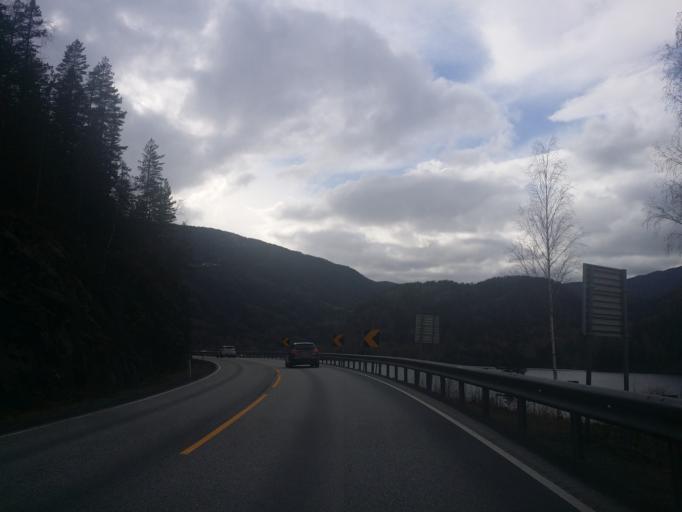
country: NO
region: Buskerud
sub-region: Nes
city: Nesbyen
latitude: 60.4879
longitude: 9.2153
